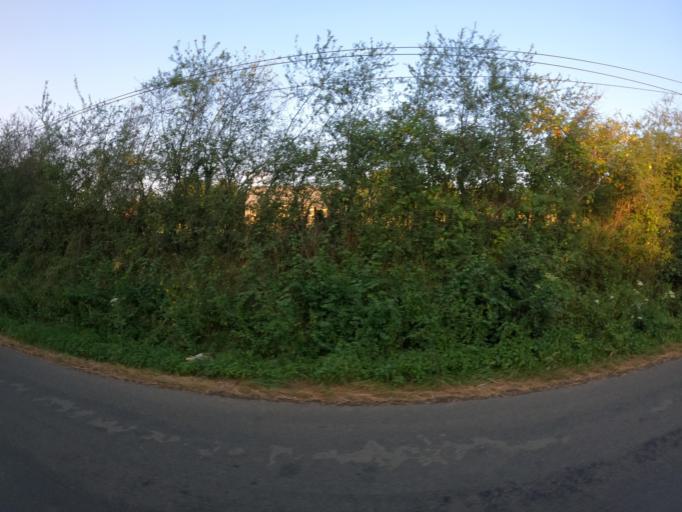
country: FR
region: Pays de la Loire
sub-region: Departement de la Sarthe
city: Parce-sur-Sarthe
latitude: 47.8820
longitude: -0.2218
